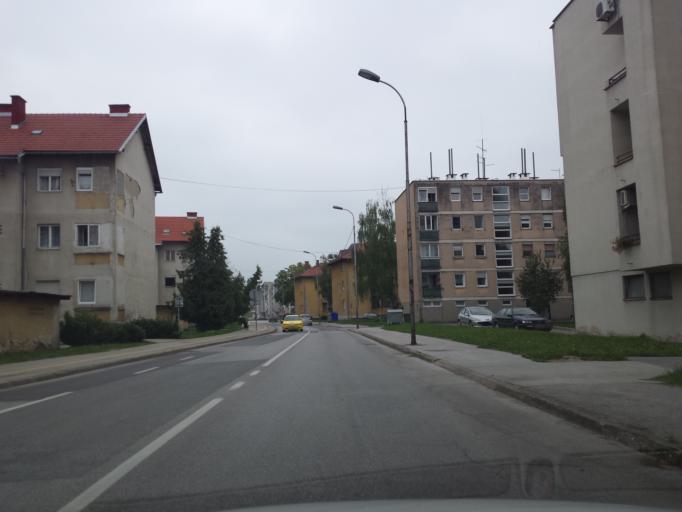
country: HR
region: Karlovacka
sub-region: Grad Karlovac
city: Karlovac
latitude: 45.4912
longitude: 15.5432
